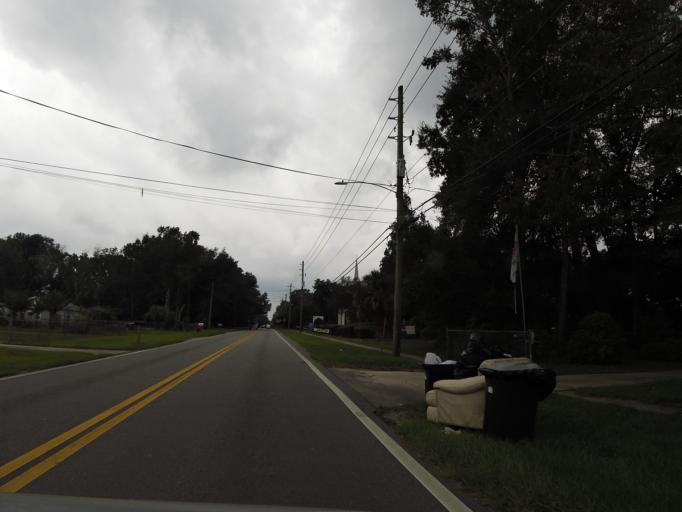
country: US
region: Florida
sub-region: Clay County
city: Bellair-Meadowbrook Terrace
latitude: 30.2425
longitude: -81.7731
